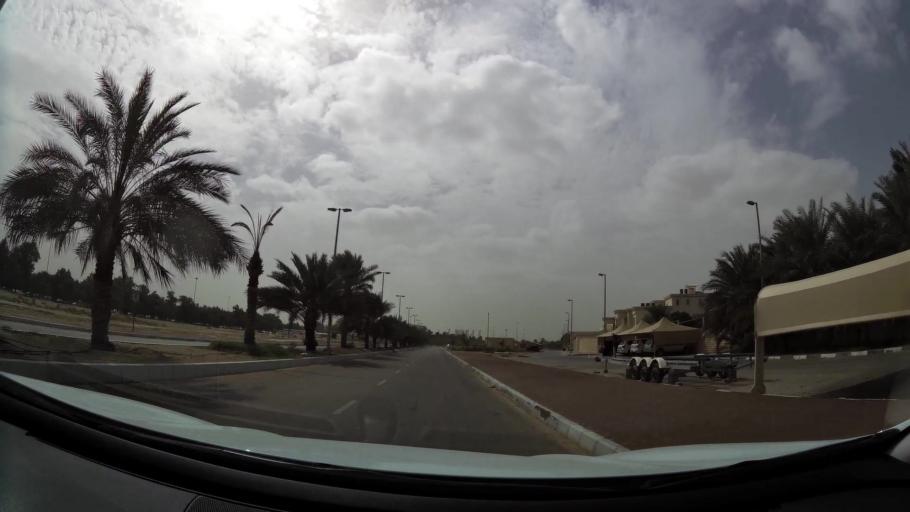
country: AE
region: Abu Dhabi
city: Abu Dhabi
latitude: 24.3996
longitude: 54.5221
